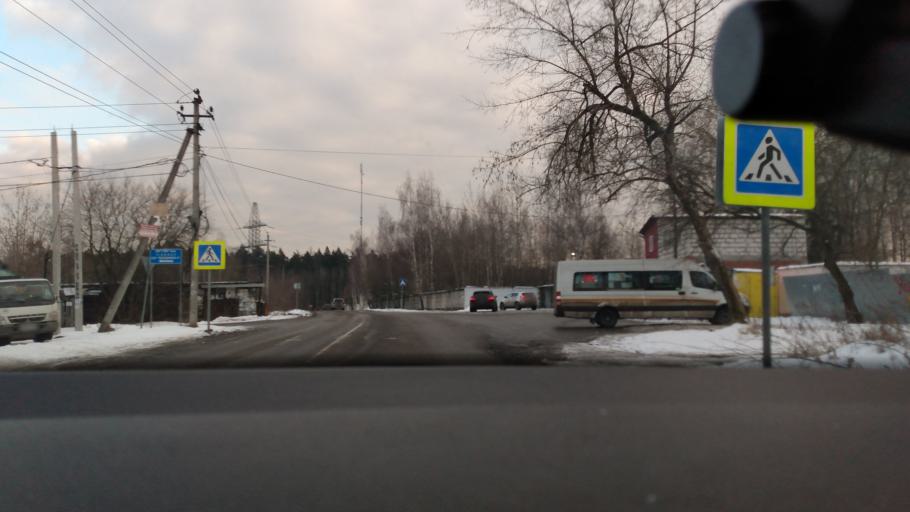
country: RU
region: Moskovskaya
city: Rodniki
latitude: 55.6901
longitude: 38.0788
